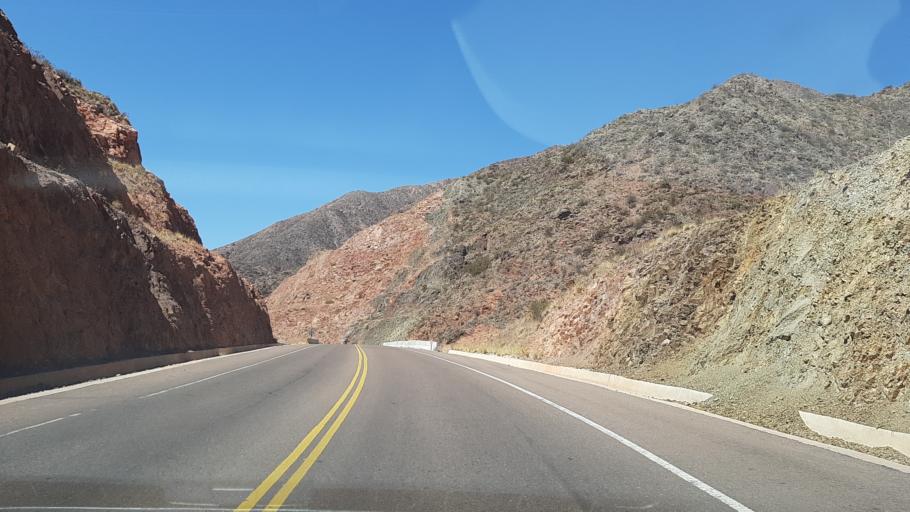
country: AR
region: Mendoza
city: Lujan de Cuyo
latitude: -32.9939
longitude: -69.1530
